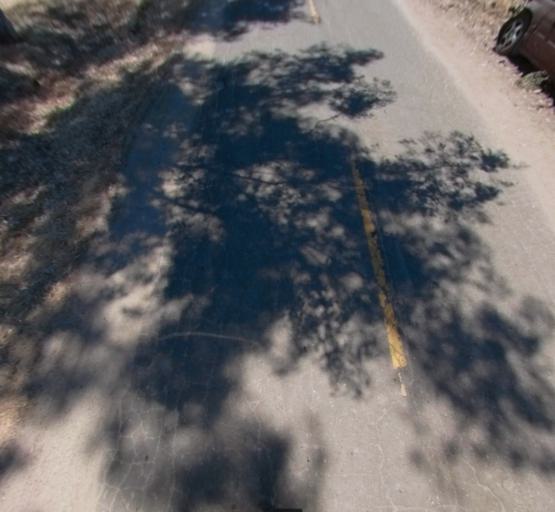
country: US
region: California
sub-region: Madera County
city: Madera
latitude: 36.9859
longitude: -120.0771
